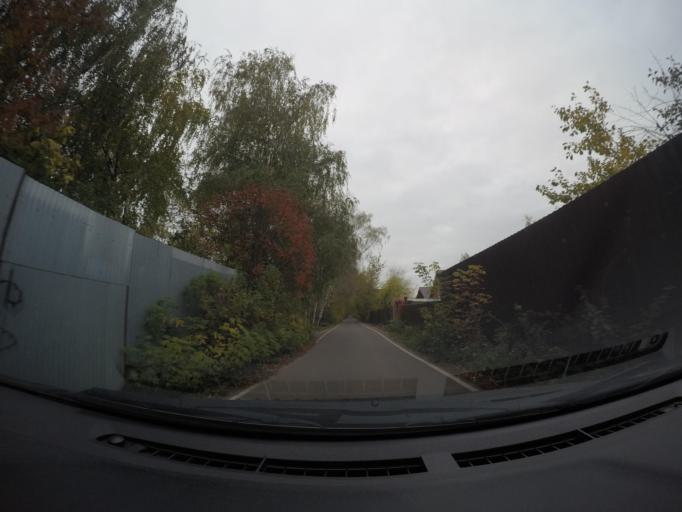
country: RU
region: Moskovskaya
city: Imeni Vorovskogo
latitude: 55.7321
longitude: 38.3082
